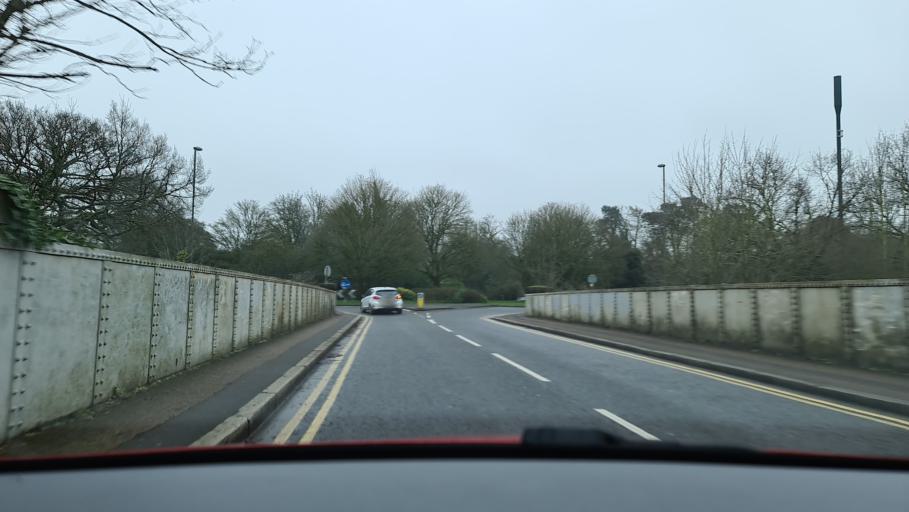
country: GB
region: England
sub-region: Surrey
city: Walton-on-Thames
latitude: 51.3713
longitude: -0.4237
